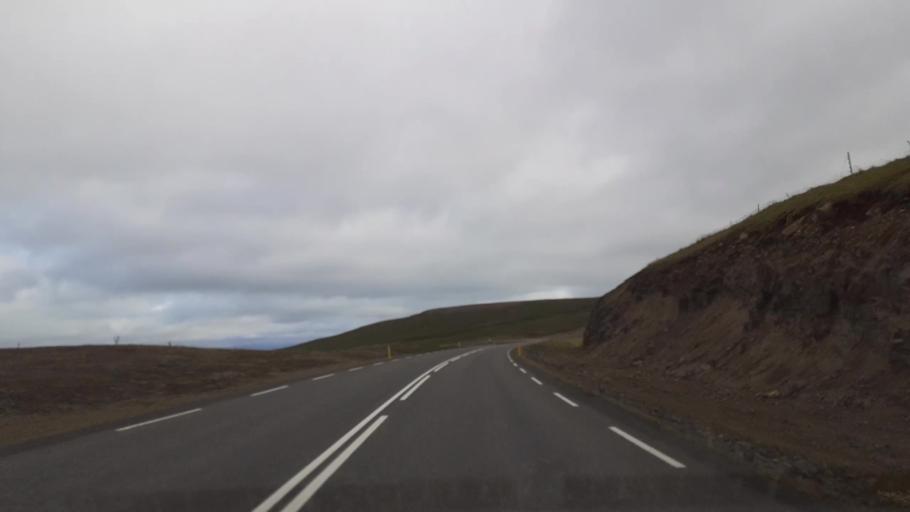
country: IS
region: Northeast
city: Husavik
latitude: 66.1997
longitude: -17.0324
